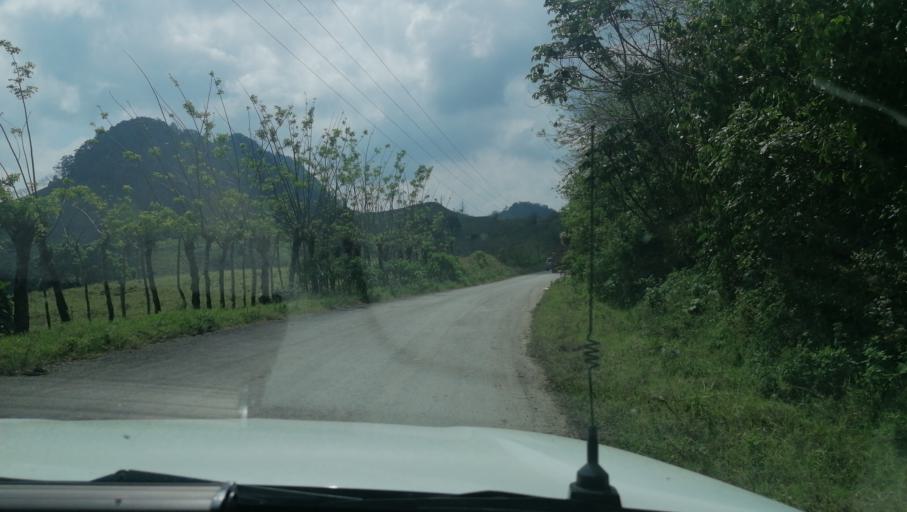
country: MX
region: Chiapas
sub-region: Francisco Leon
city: San Miguel la Sardina
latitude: 17.2521
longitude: -93.2768
